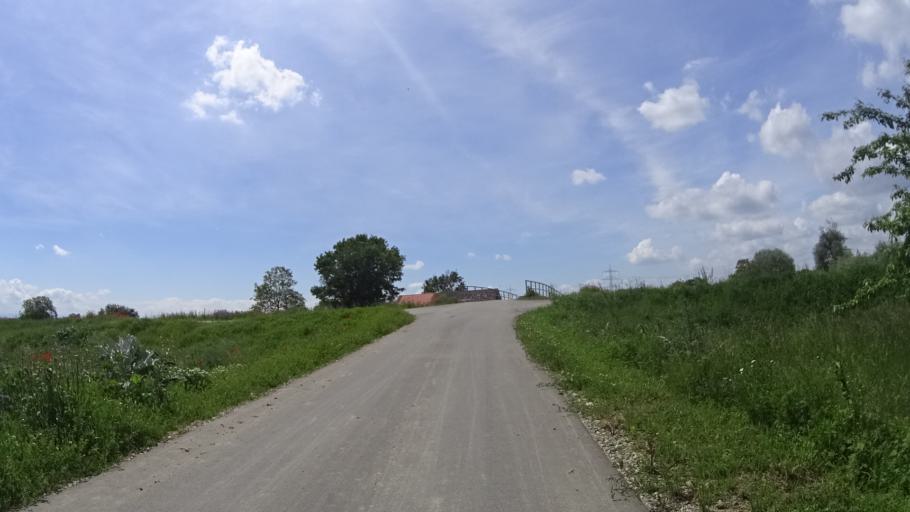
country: DE
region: Baden-Wuerttemberg
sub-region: Freiburg Region
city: Schwanau
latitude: 48.3580
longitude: 7.7565
